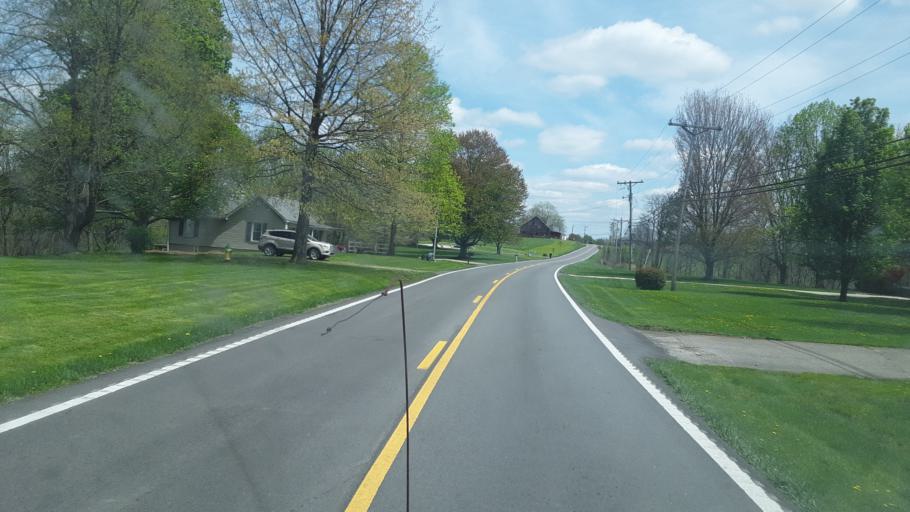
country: US
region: Kentucky
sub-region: Grant County
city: Dry Ridge
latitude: 38.6789
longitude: -84.6197
